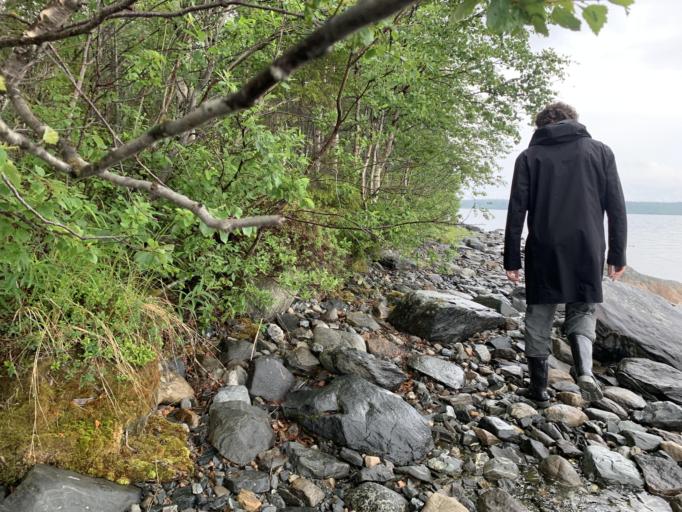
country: RU
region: Murmansk
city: Monchegorsk
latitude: 67.6899
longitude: 32.9710
